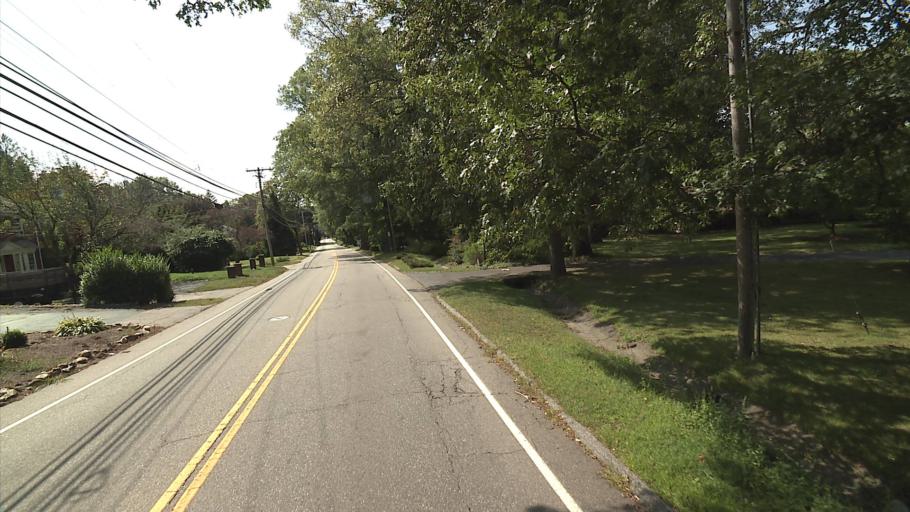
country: US
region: Connecticut
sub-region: New London County
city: Norwich
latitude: 41.5547
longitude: -72.0792
